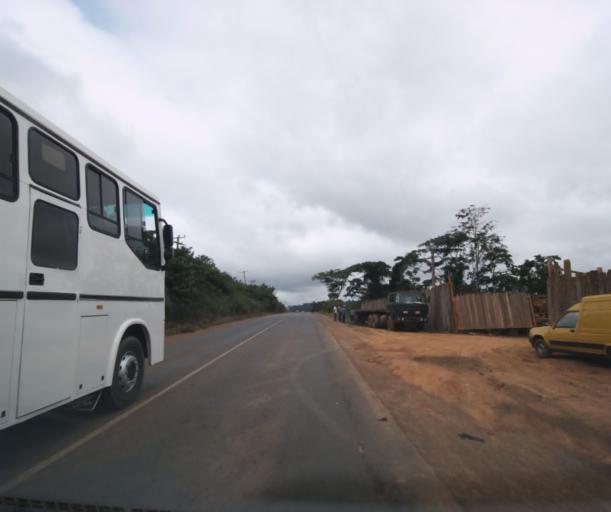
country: CM
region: Centre
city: Mbankomo
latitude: 3.7845
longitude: 11.4614
